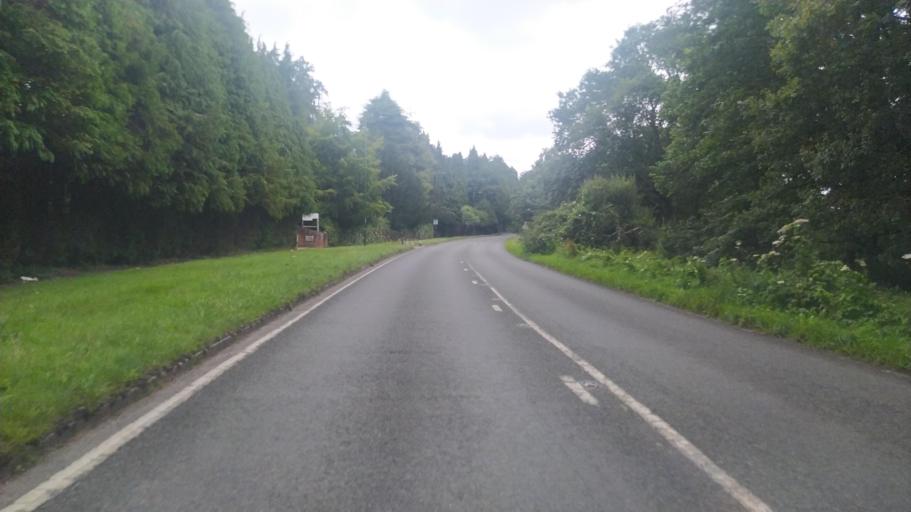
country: GB
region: England
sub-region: Hampshire
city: Liss
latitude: 51.0395
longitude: -0.8643
